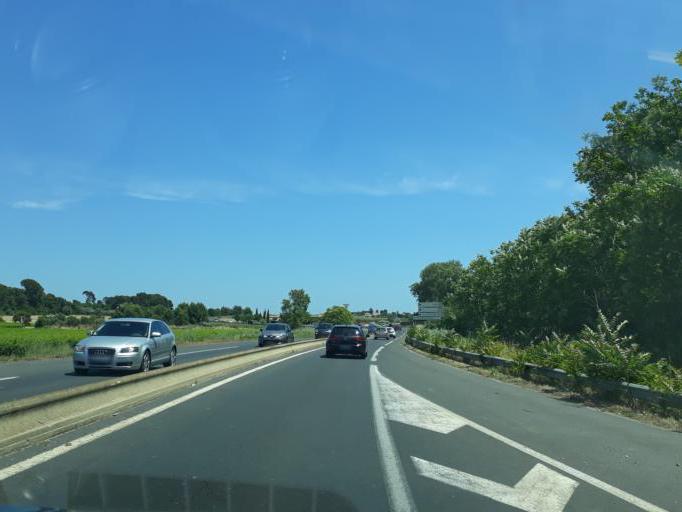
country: FR
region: Languedoc-Roussillon
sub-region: Departement de l'Herault
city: Cers
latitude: 43.3161
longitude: 3.3104
